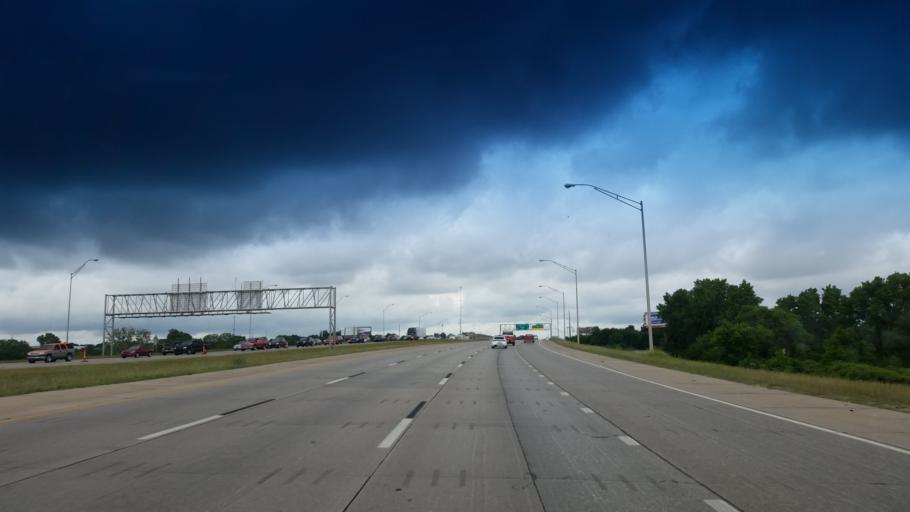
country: US
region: Oklahoma
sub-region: Oklahoma County
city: Oklahoma City
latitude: 35.4565
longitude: -97.4909
